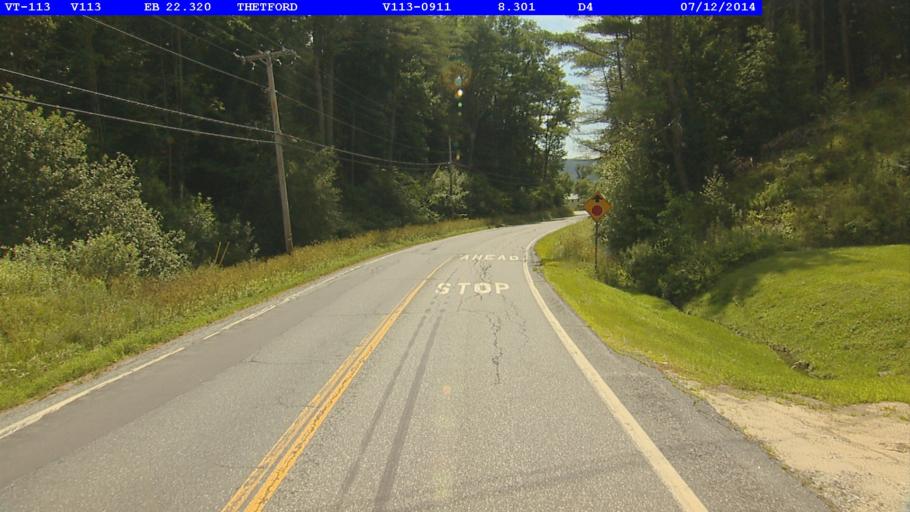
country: US
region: New Hampshire
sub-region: Grafton County
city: Lyme
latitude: 43.8137
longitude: -72.1926
